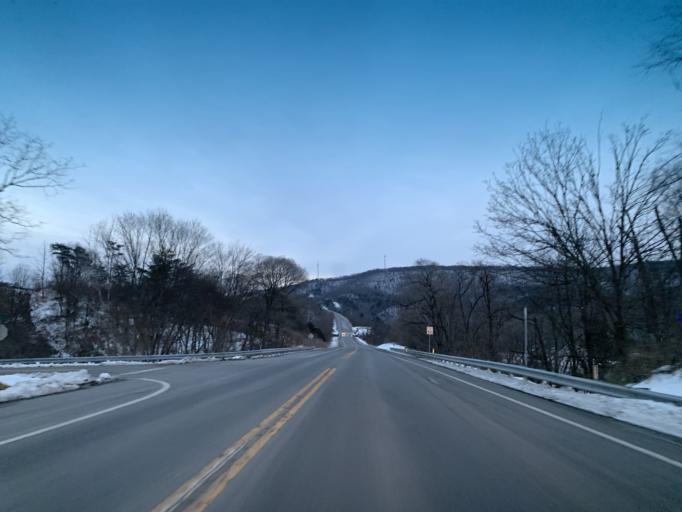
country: US
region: Maryland
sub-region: Allegany County
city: Cumberland
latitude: 39.6962
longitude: -78.5532
